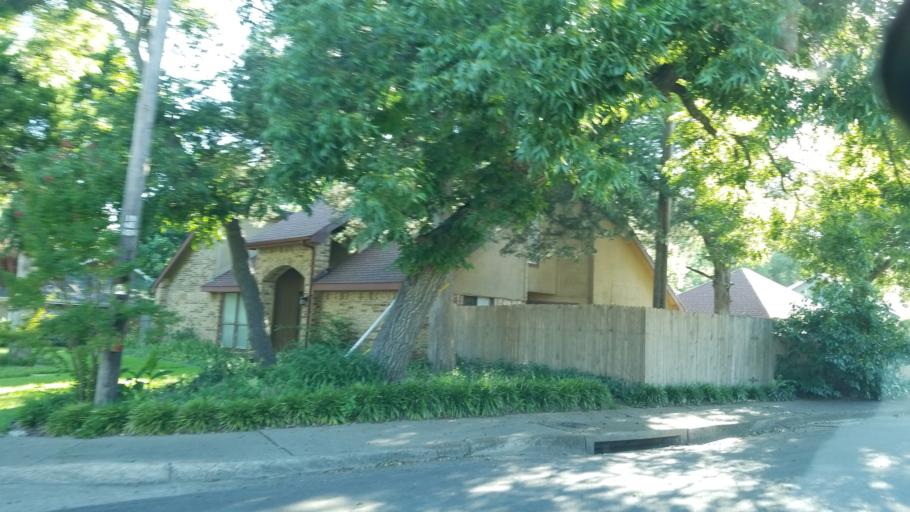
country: US
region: Texas
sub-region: Dallas County
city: Balch Springs
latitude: 32.7804
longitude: -96.7066
